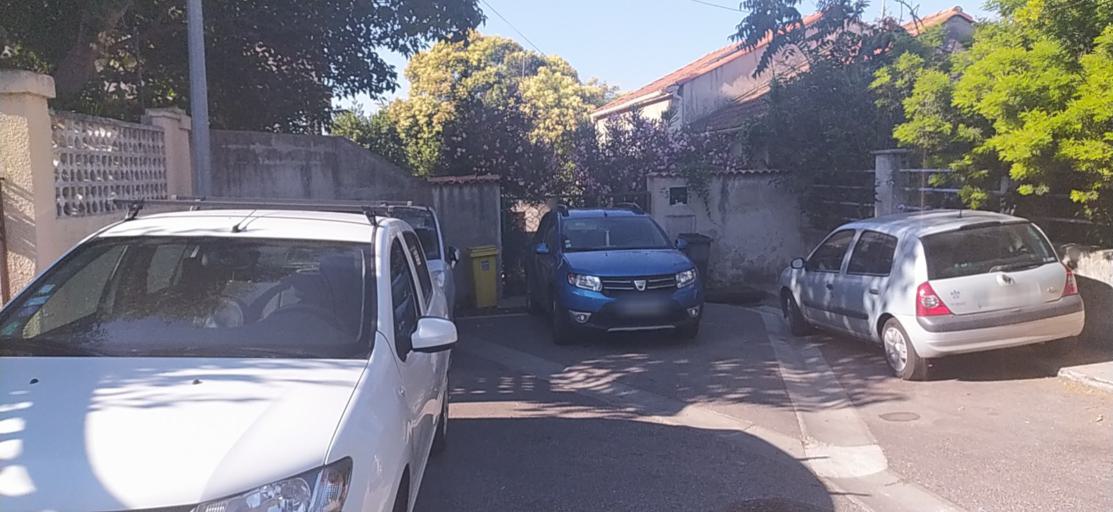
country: FR
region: Provence-Alpes-Cote d'Azur
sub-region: Departement des Bouches-du-Rhone
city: Marseille 14
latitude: 43.3391
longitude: 5.3529
